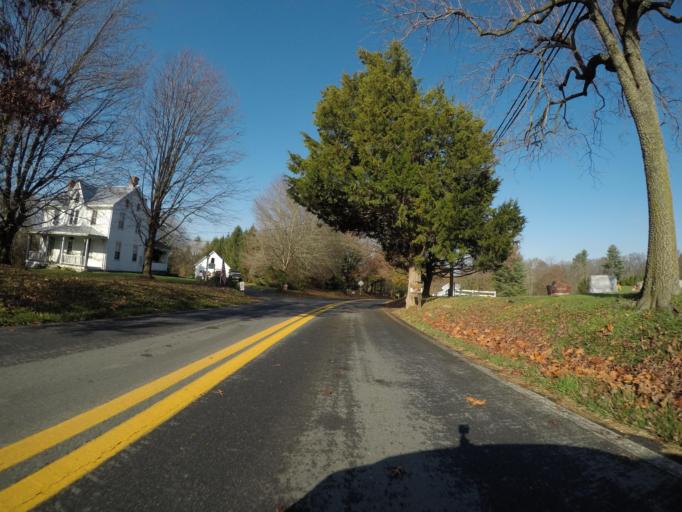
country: US
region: Maryland
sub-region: Baltimore County
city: Reisterstown
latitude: 39.5304
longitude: -76.8583
